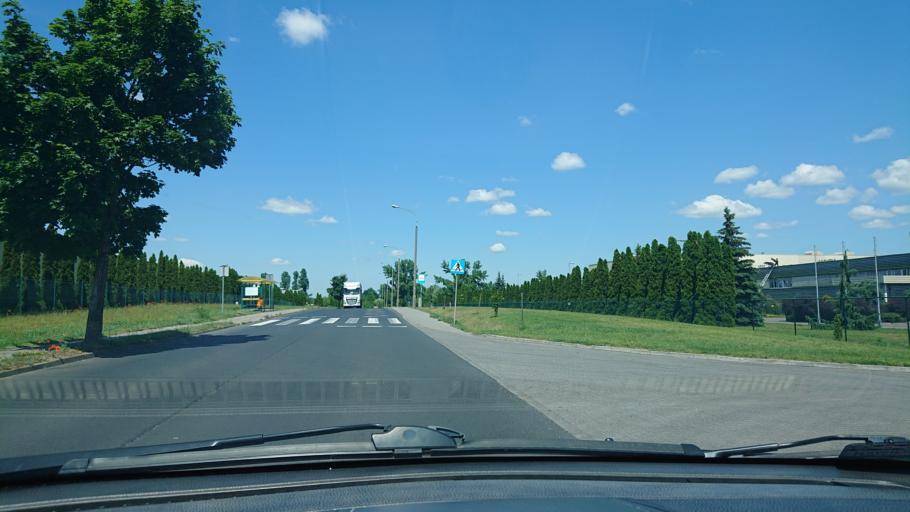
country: PL
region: Greater Poland Voivodeship
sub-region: Powiat gnieznienski
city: Gniezno
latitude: 52.5264
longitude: 17.6186
